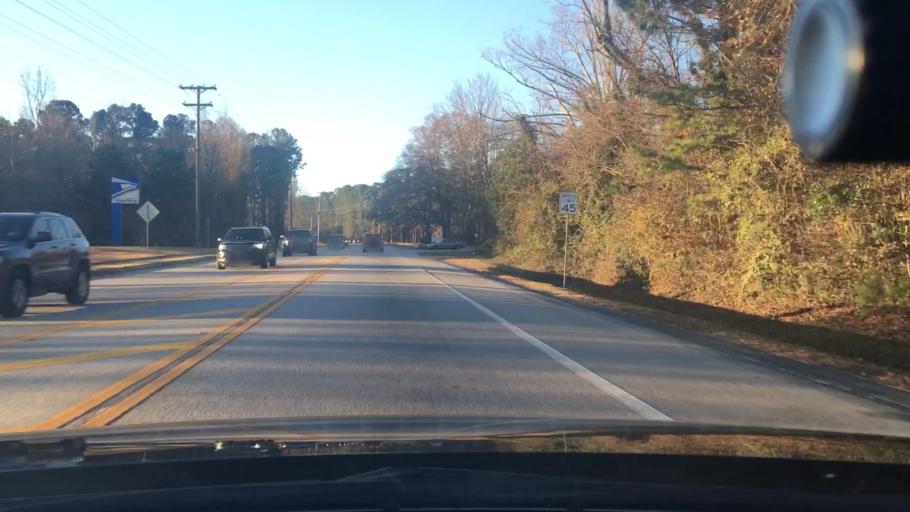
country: US
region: Georgia
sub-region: Fayette County
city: Peachtree City
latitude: 33.3403
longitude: -84.6462
